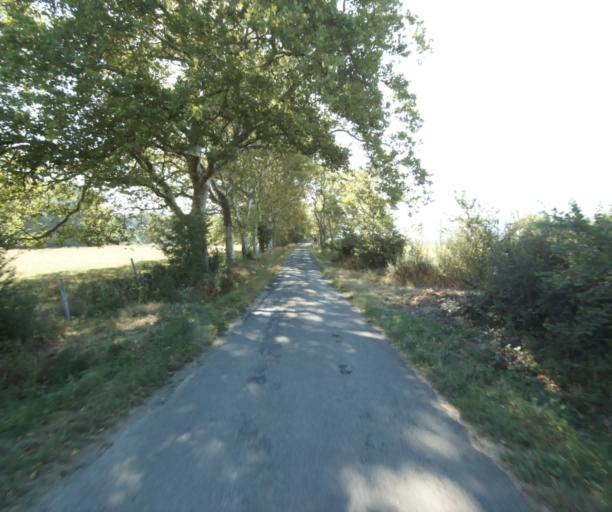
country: FR
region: Midi-Pyrenees
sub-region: Departement de la Haute-Garonne
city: Revel
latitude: 43.4641
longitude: 2.0183
